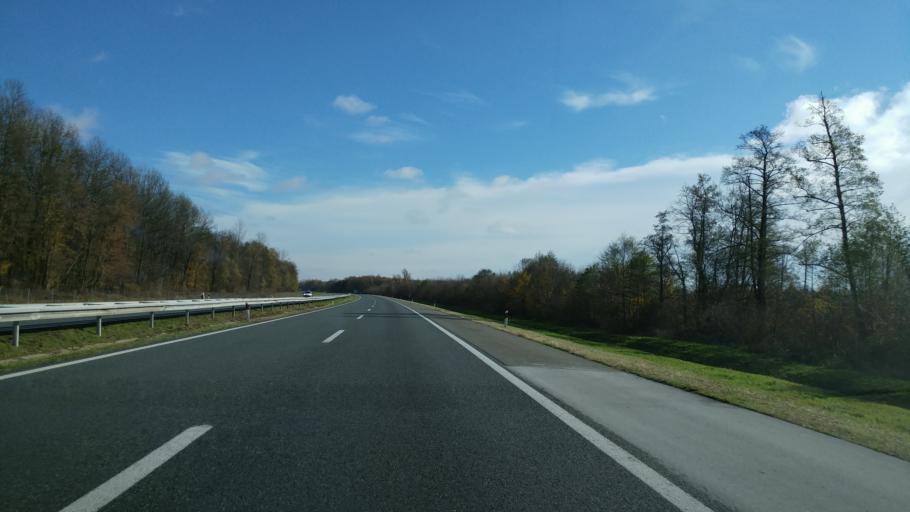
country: HR
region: Sisacko-Moslavacka
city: Novska
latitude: 45.3138
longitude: 16.9856
